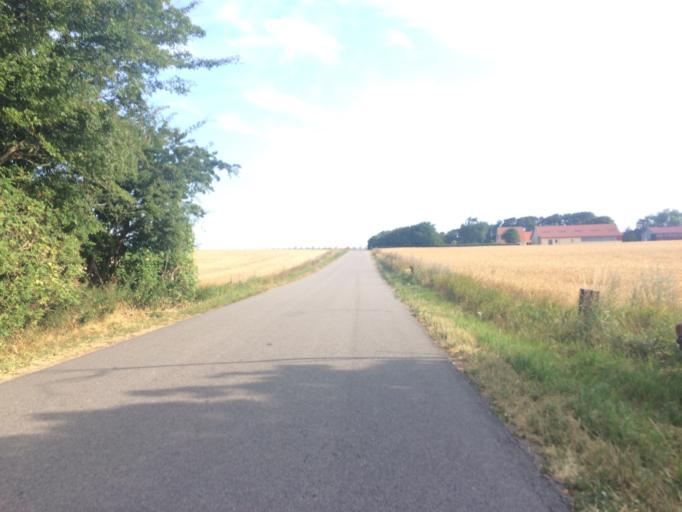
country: DK
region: Central Jutland
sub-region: Holstebro Kommune
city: Vinderup
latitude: 56.5725
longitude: 8.7570
